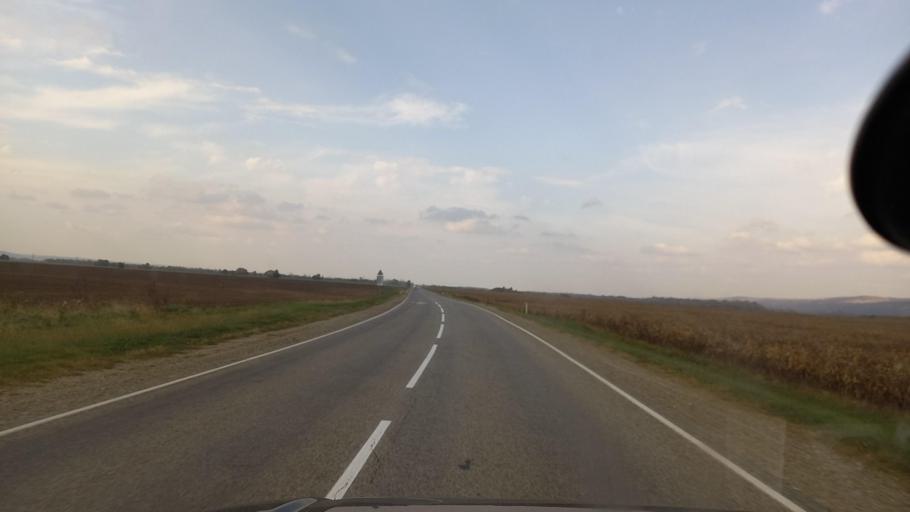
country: RU
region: Krasnodarskiy
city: Perepravnaya
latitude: 44.3497
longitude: 40.8400
